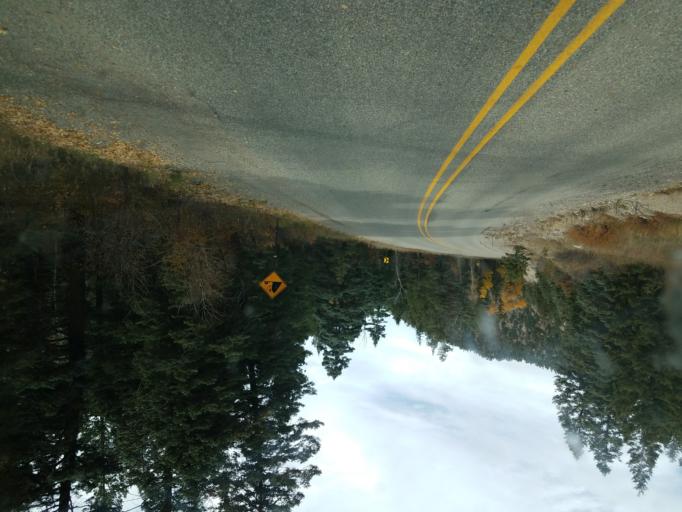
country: US
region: New Mexico
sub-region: Taos County
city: Arroyo Seco
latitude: 36.5543
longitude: -105.5385
